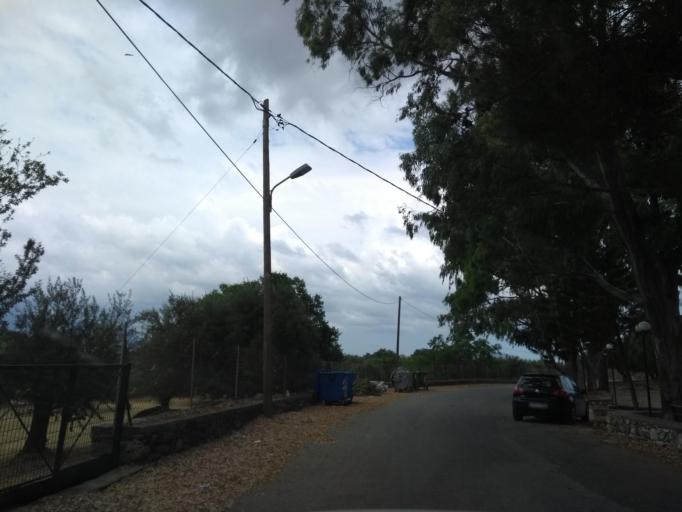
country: GR
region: Crete
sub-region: Nomos Chanias
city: Georgioupolis
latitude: 35.4032
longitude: 24.2190
